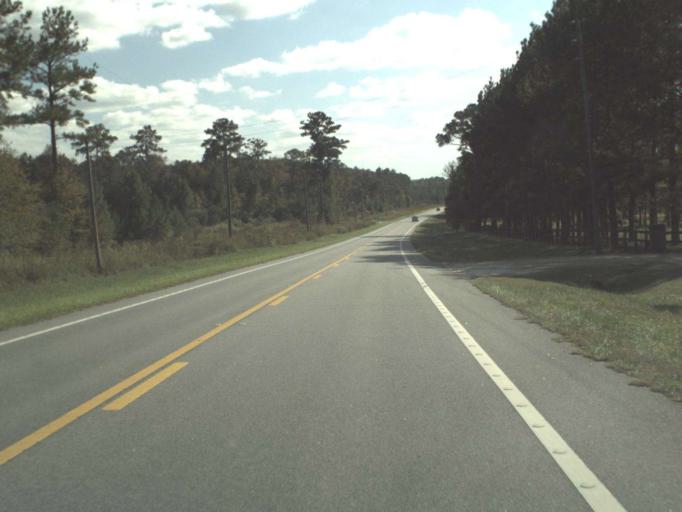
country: US
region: Florida
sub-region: Jefferson County
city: Monticello
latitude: 30.4535
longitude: -84.0187
